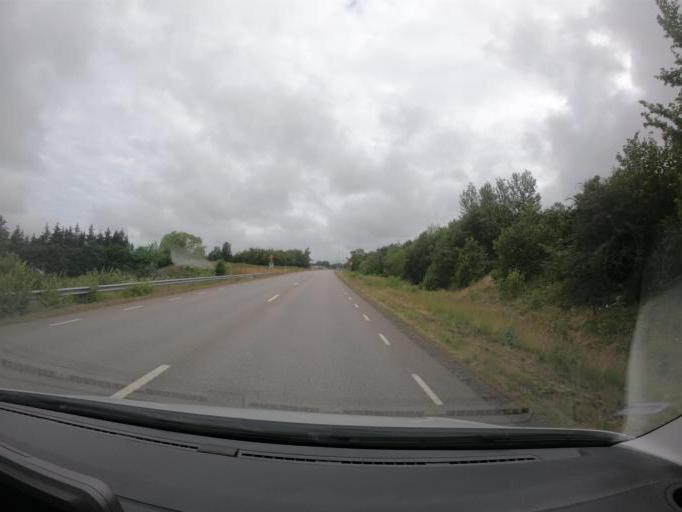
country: SE
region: Skane
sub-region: Bastads Kommun
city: Forslov
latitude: 56.3652
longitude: 12.7985
